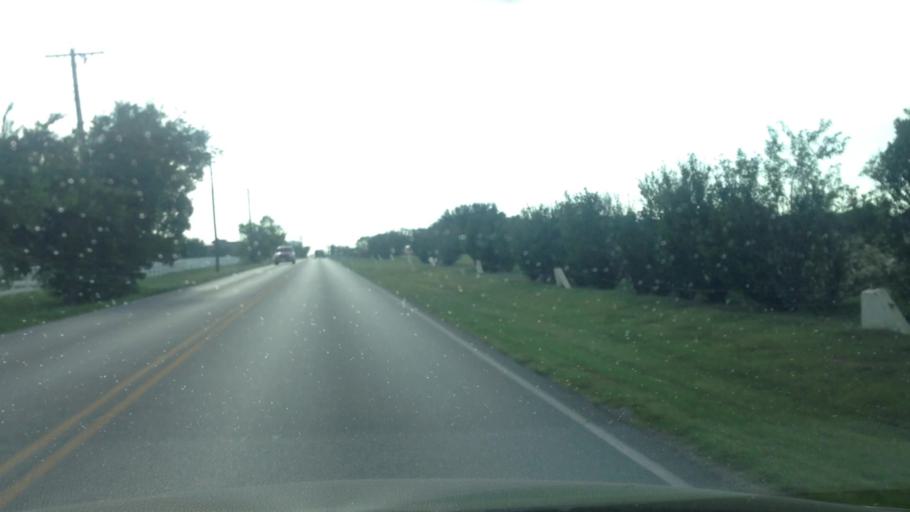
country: US
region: Texas
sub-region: Tarrant County
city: Haslet
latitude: 32.9689
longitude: -97.3925
